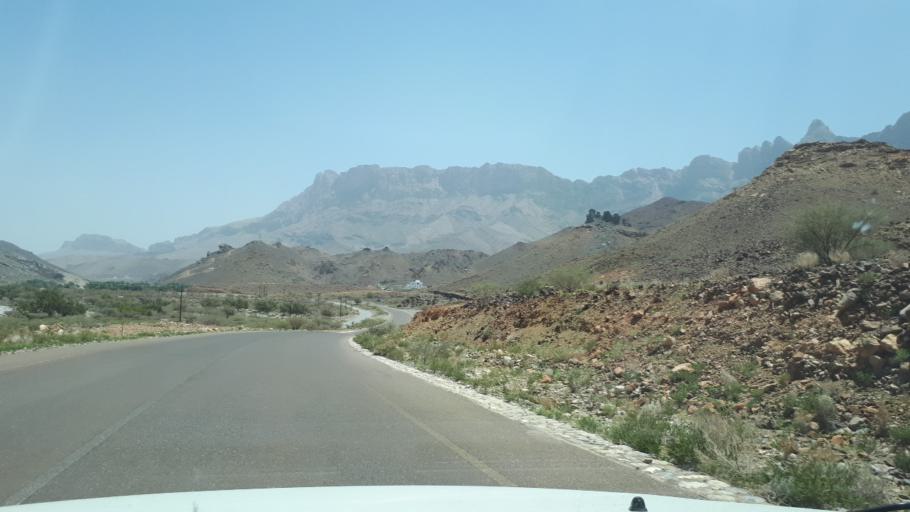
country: OM
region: Muhafazat ad Dakhiliyah
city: Bahla'
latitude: 23.1785
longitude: 57.1441
